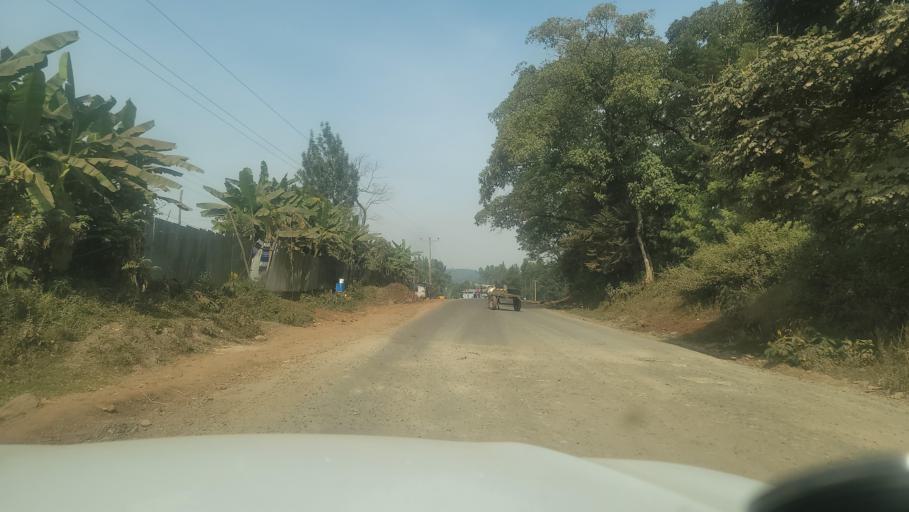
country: ET
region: Oromiya
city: Jima
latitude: 7.7018
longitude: 36.8074
